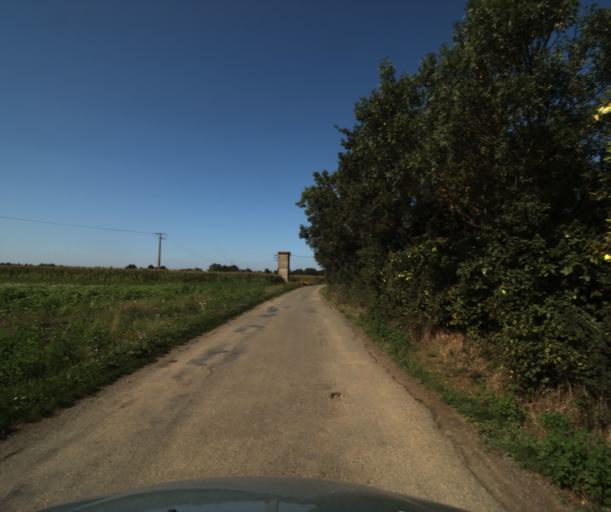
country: FR
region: Midi-Pyrenees
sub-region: Departement de la Haute-Garonne
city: Lacasse
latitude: 43.3821
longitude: 1.2563
